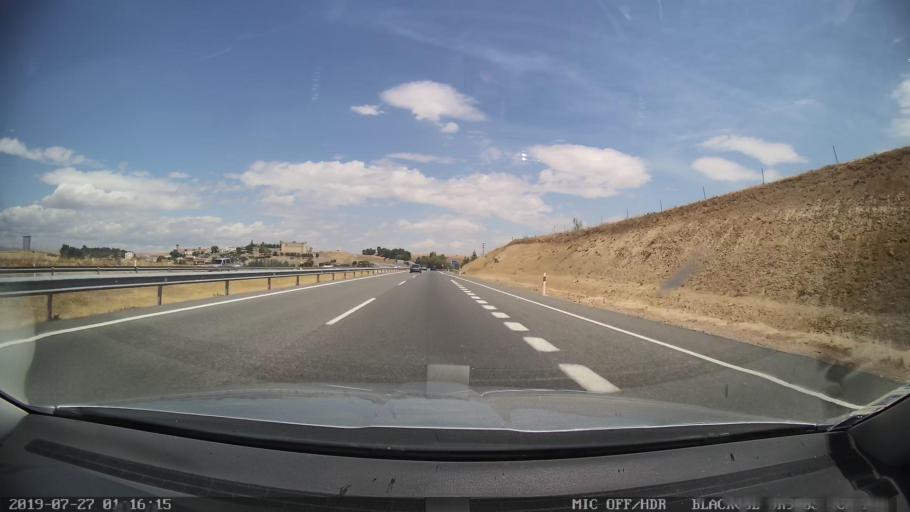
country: ES
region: Castille-La Mancha
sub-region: Province of Toledo
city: Maqueda
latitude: 40.0582
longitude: -4.3732
